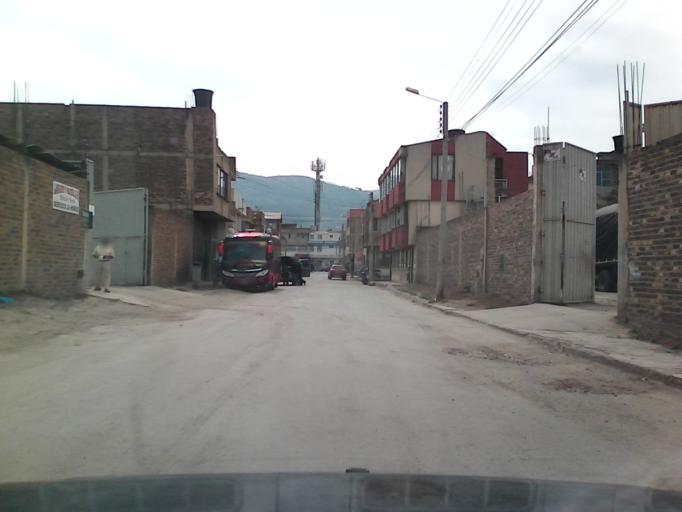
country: CO
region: Boyaca
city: Sogamoso
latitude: 5.7208
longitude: -72.9363
